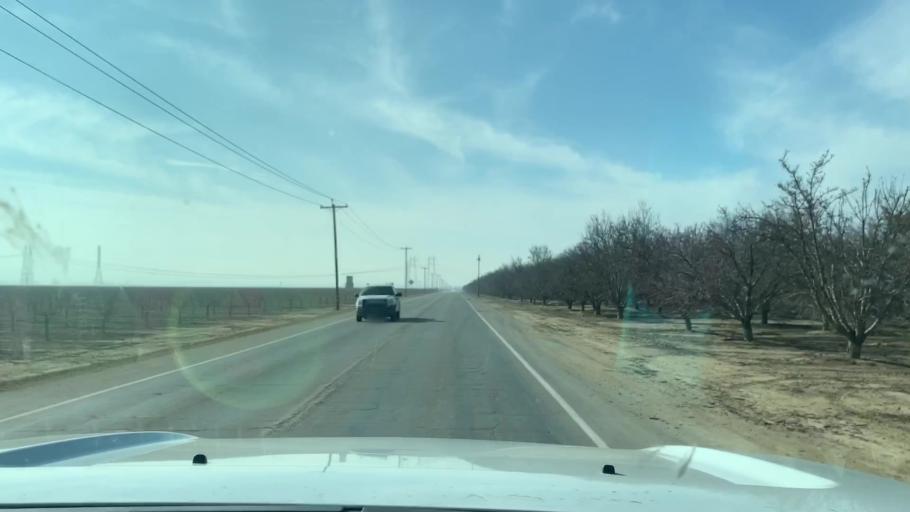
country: US
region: California
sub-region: Kern County
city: Buttonwillow
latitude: 35.4424
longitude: -119.4752
